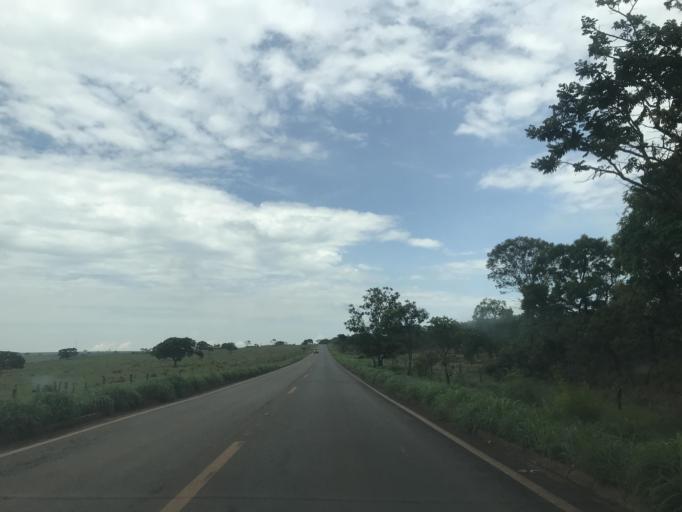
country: BR
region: Goias
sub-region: Luziania
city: Luziania
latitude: -16.2706
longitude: -47.9864
